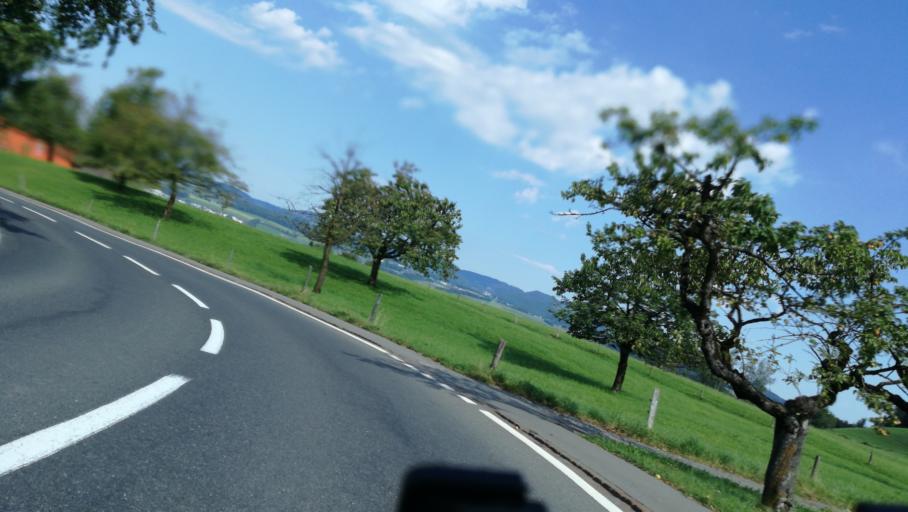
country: CH
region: Zug
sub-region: Zug
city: Baar
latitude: 47.1730
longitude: 8.5526
